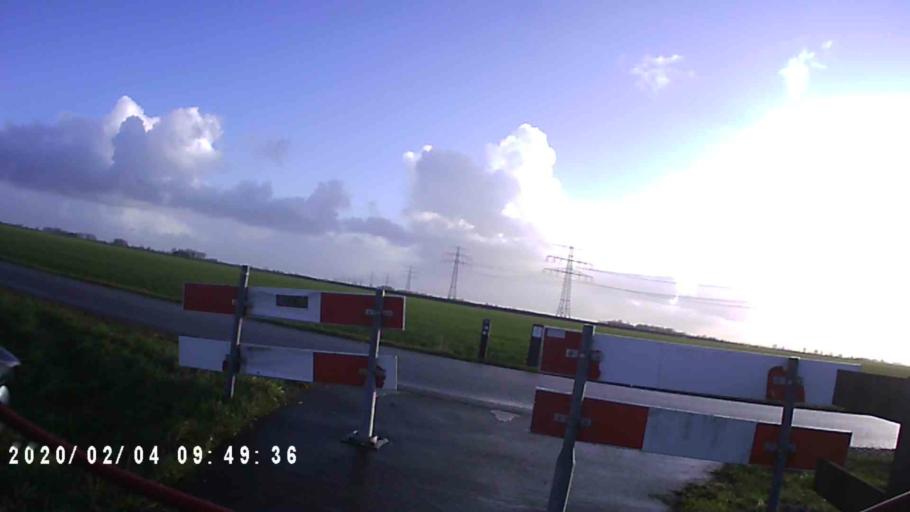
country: NL
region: Groningen
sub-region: Gemeente Winsum
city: Winsum
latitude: 53.2908
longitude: 6.4938
